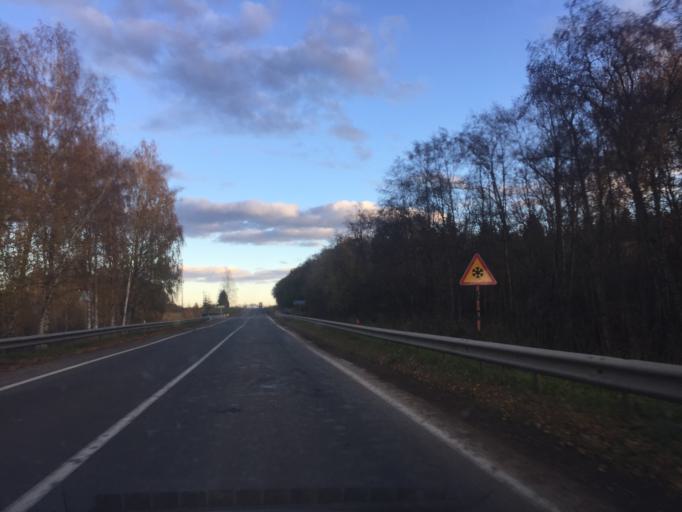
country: BY
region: Vitebsk
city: Myory
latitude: 55.8189
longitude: 27.6508
